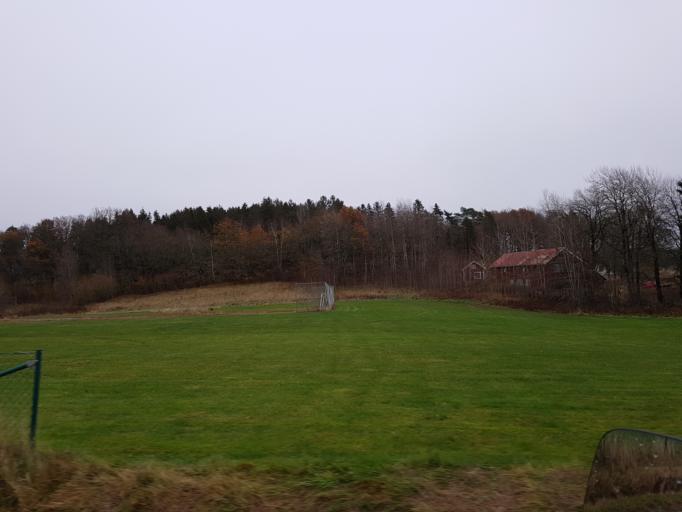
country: SE
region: Vaestra Goetaland
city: Svanesund
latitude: 58.2053
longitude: 11.7756
